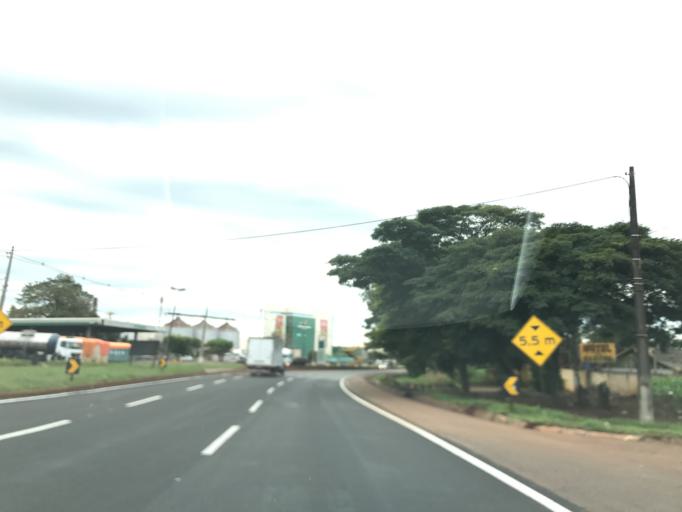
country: BR
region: Parana
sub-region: Rolandia
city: Rolandia
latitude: -23.3577
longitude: -51.3955
